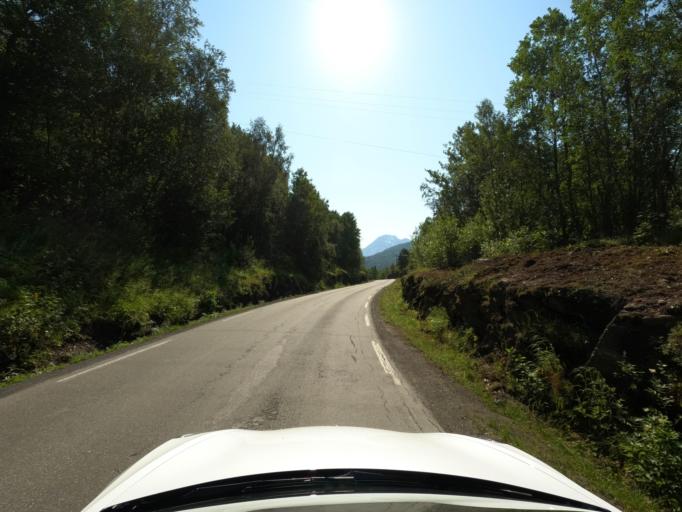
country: NO
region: Nordland
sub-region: Narvik
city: Narvik
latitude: 68.3713
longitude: 17.2514
